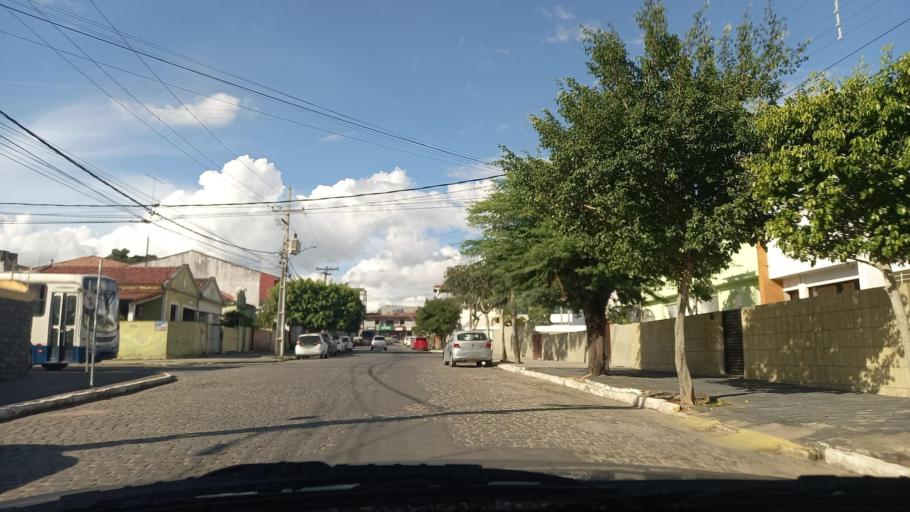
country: BR
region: Pernambuco
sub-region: Gravata
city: Gravata
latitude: -8.2012
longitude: -35.5645
